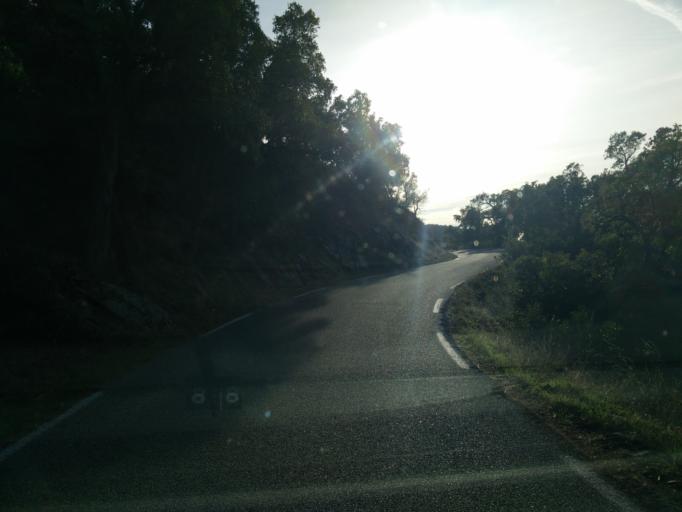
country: FR
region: Provence-Alpes-Cote d'Azur
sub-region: Departement du Var
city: Collobrieres
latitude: 43.1903
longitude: 6.3179
